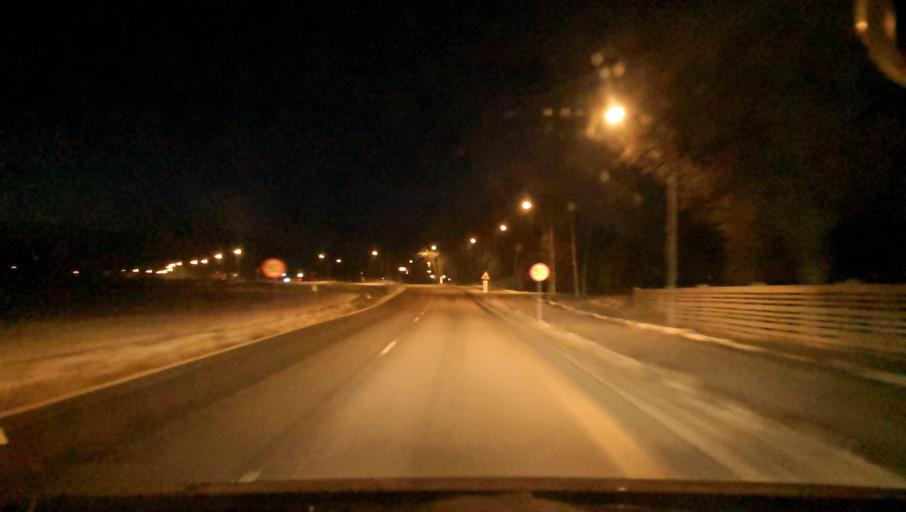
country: SE
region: Soedermanland
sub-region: Eskilstuna Kommun
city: Skogstorp
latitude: 59.2901
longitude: 16.4630
